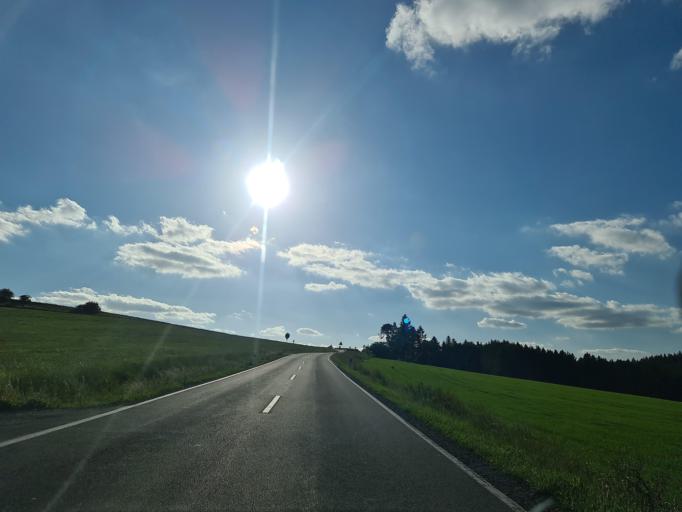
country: DE
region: Saxony
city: Reuth
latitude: 50.4728
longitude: 11.9697
